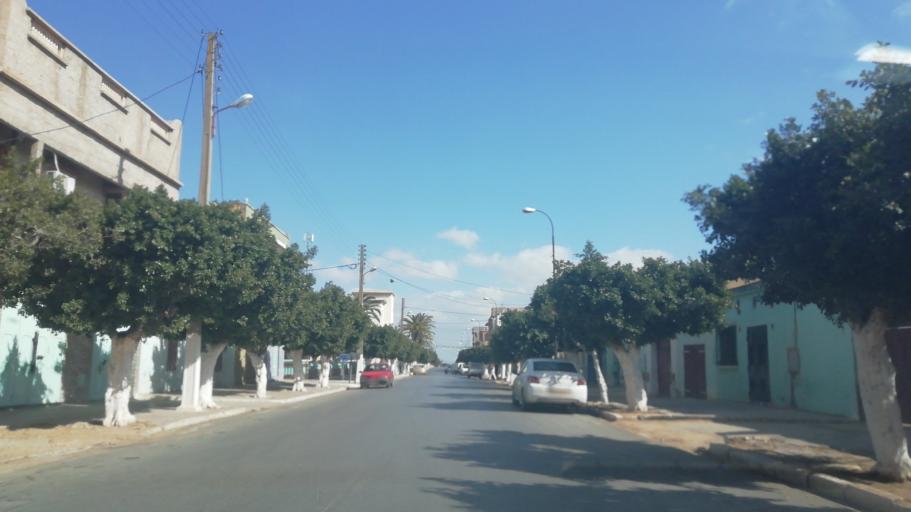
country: DZ
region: Mostaganem
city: Mostaganem
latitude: 35.9999
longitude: 0.3379
